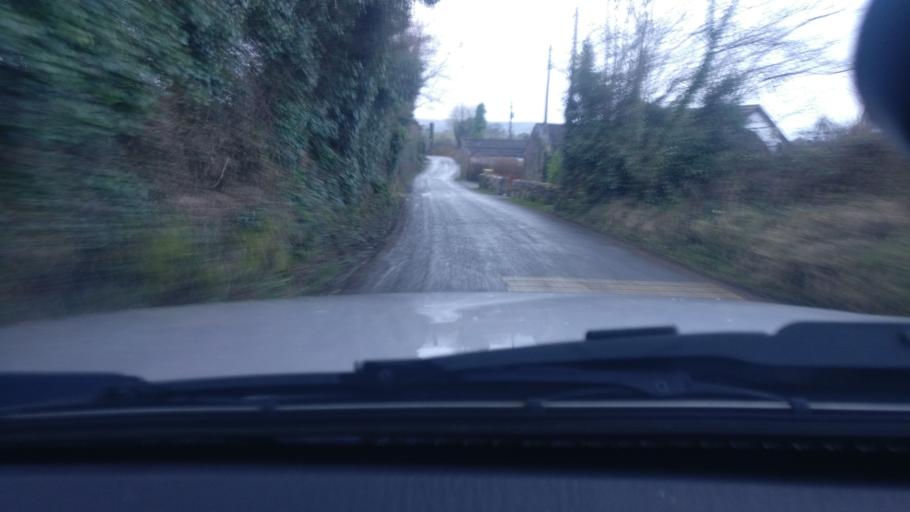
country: IE
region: Connaught
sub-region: County Galway
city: Loughrea
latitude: 53.1636
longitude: -8.5661
